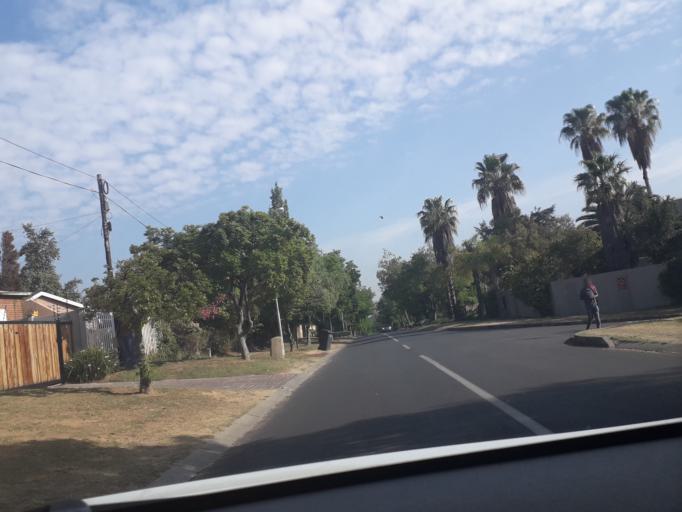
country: ZA
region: Gauteng
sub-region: City of Johannesburg Metropolitan Municipality
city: Diepsloot
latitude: -26.0491
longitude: 27.9841
